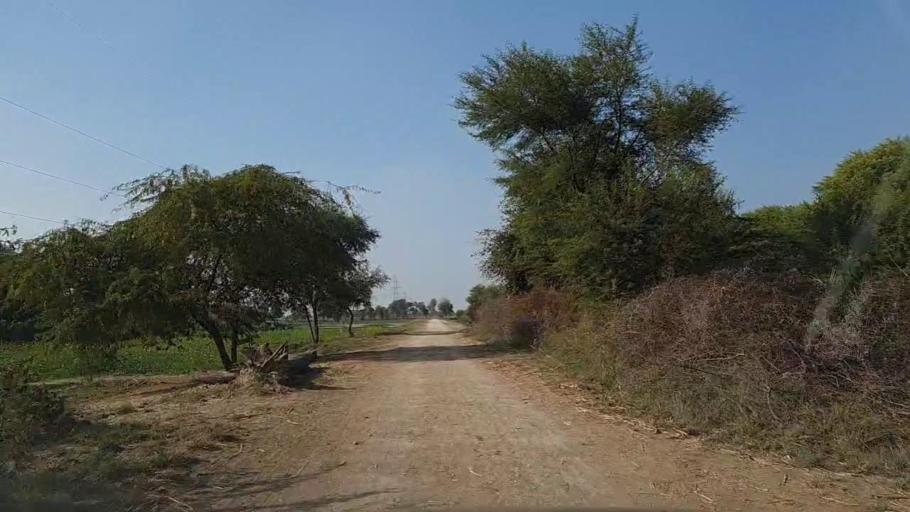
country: PK
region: Sindh
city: Daur
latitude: 26.3826
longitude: 68.3285
